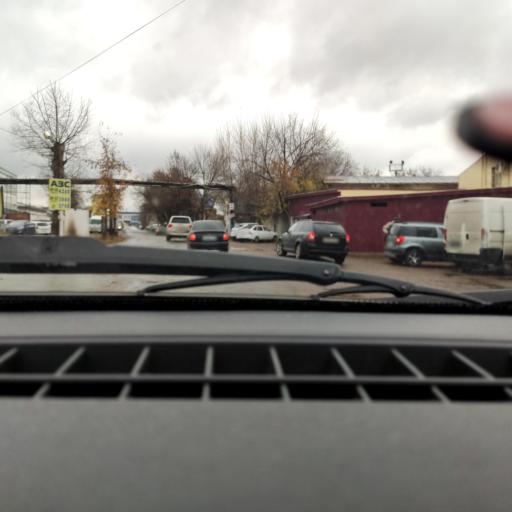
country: RU
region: Bashkortostan
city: Ufa
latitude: 54.7836
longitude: 56.0608
